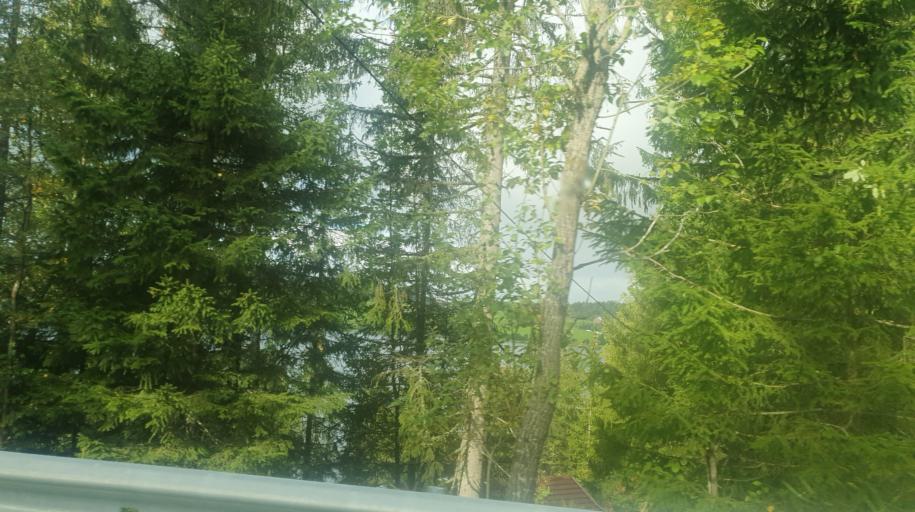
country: NO
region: Nord-Trondelag
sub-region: Levanger
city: Skogn
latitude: 63.6184
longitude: 11.1878
